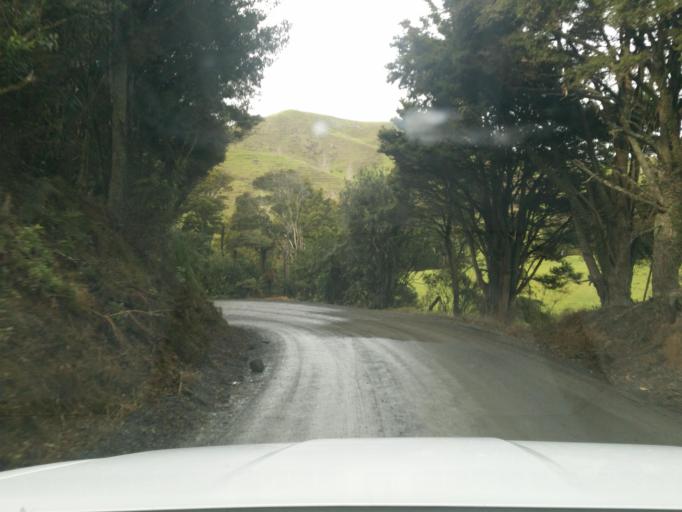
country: NZ
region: Northland
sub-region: Kaipara District
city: Dargaville
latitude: -35.8307
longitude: 173.8241
